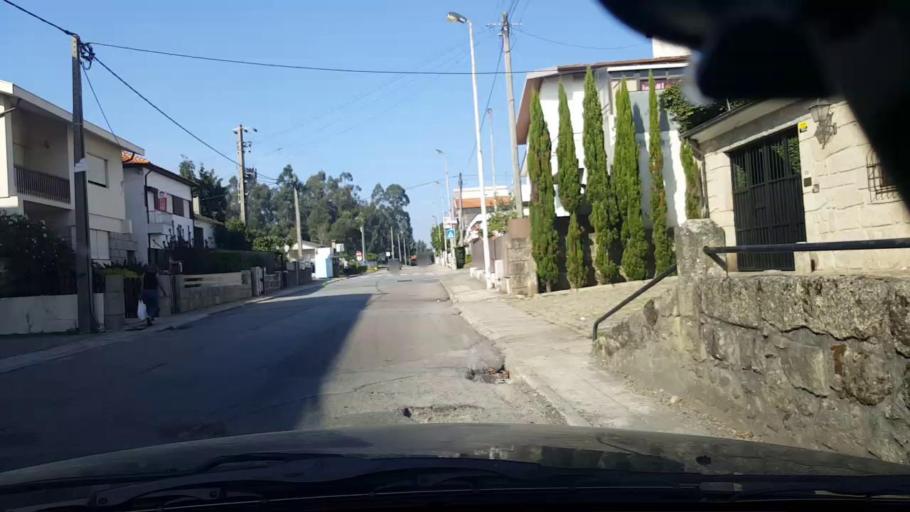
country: PT
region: Porto
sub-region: Maia
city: Gemunde
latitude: 41.2711
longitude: -8.6798
